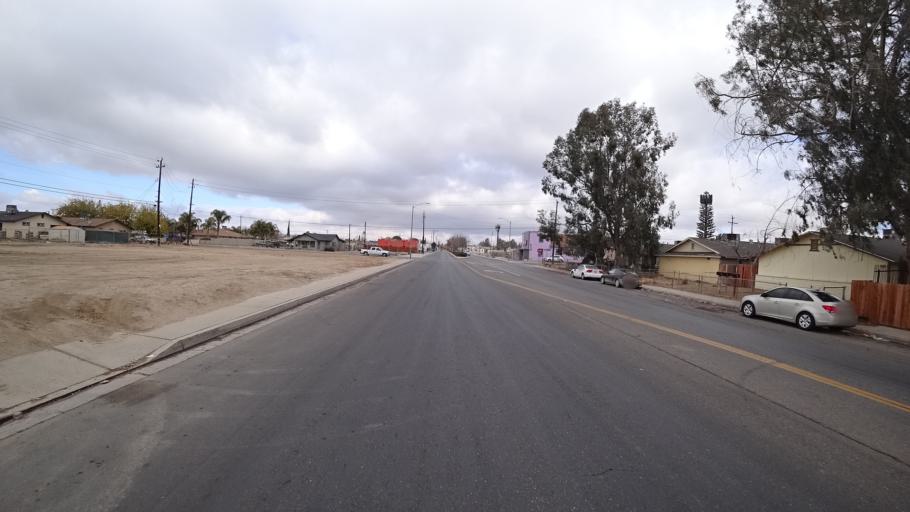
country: US
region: California
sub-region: Kern County
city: Bakersfield
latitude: 35.3606
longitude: -118.9853
